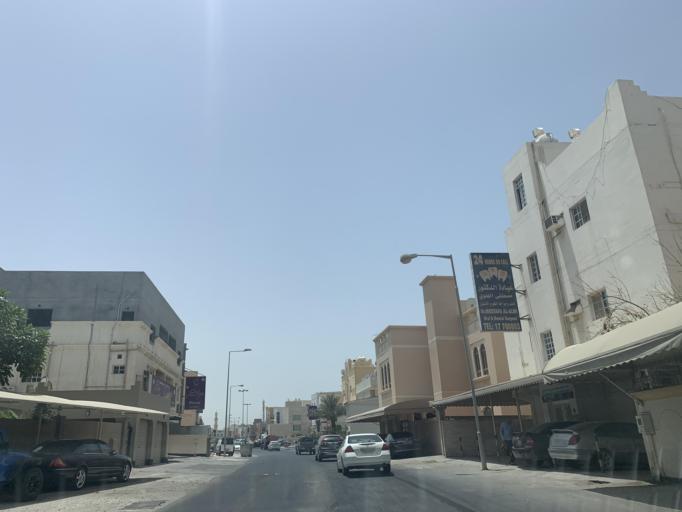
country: BH
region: Northern
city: Madinat `Isa
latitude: 26.1713
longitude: 50.5658
